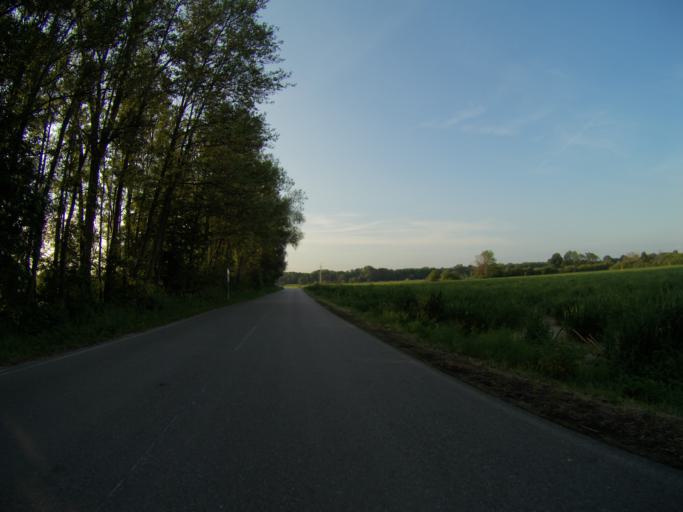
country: DE
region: Bavaria
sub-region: Upper Bavaria
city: Marzling
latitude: 48.3932
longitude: 11.7976
